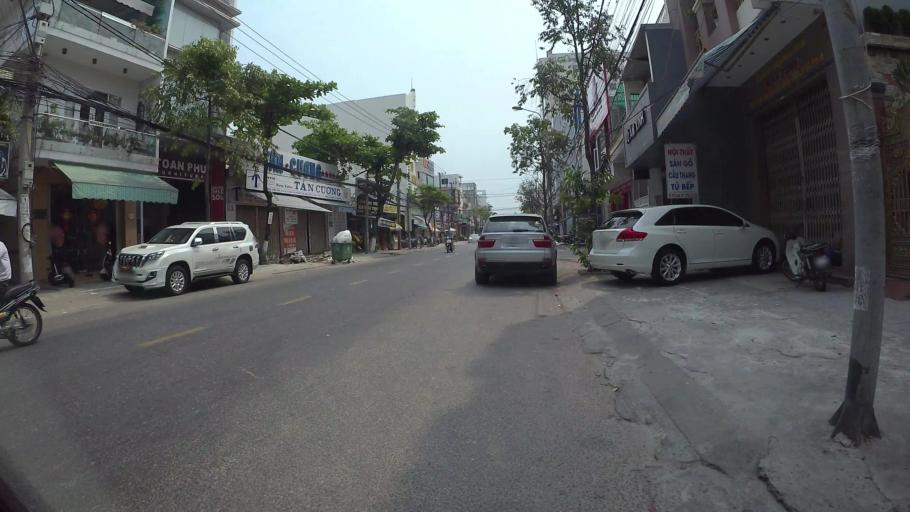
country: VN
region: Da Nang
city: Son Tra
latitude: 16.0519
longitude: 108.2202
